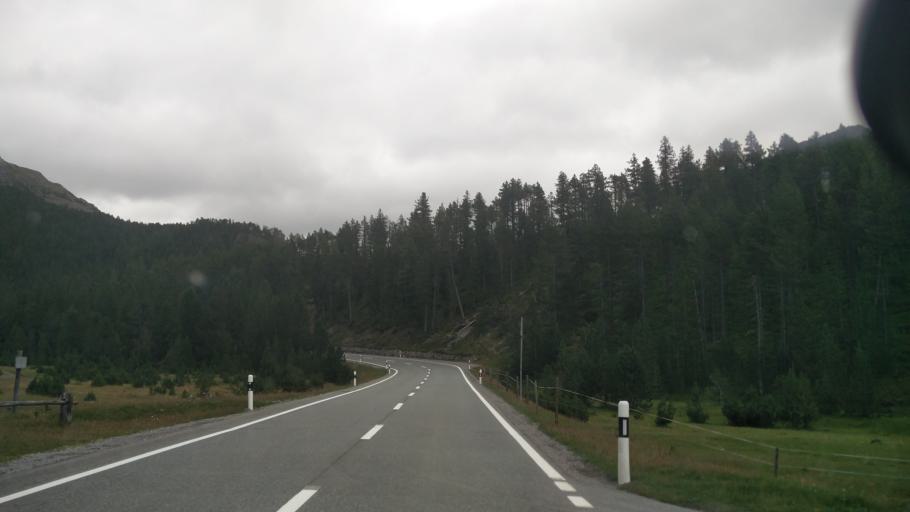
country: CH
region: Grisons
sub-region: Inn District
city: Scuol
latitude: 46.6464
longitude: 10.2710
